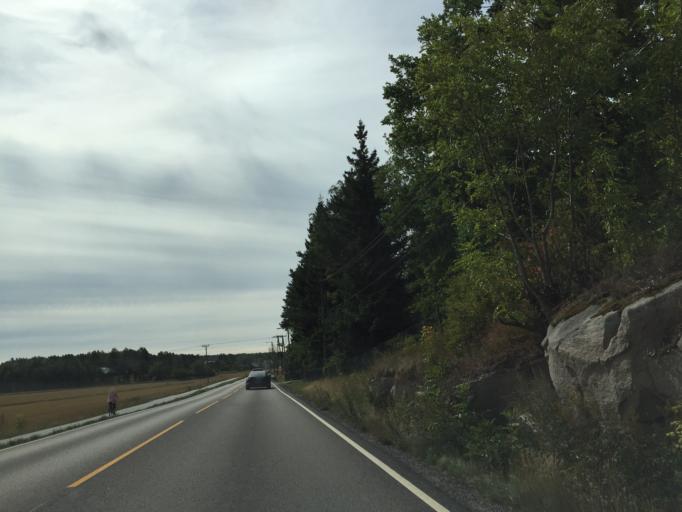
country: NO
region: Ostfold
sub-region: Fredrikstad
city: Fredrikstad
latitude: 59.1748
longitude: 10.9328
